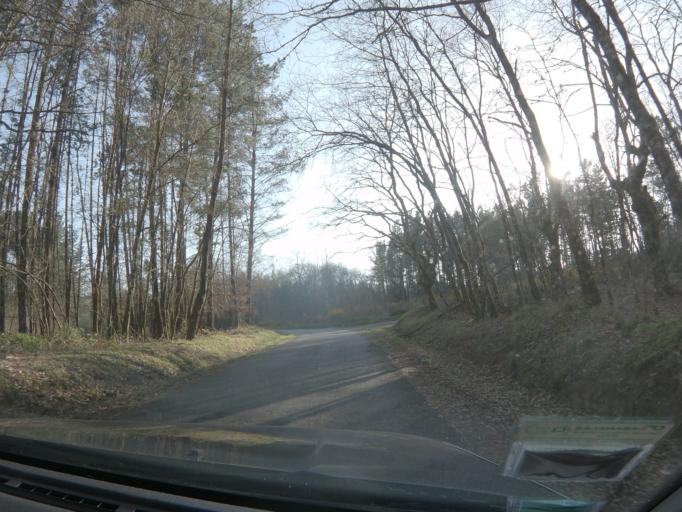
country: ES
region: Galicia
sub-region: Provincia de Lugo
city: Corgo
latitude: 42.9363
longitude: -7.4468
